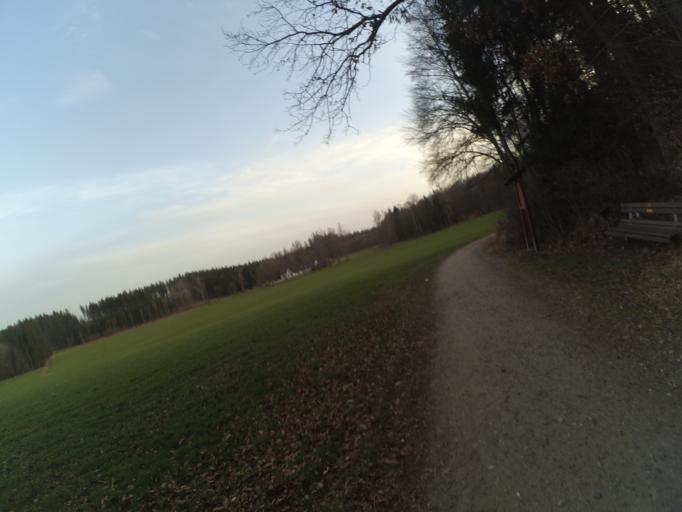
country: DE
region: Bavaria
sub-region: Swabia
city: Bad Worishofen
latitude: 47.9974
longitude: 10.5688
